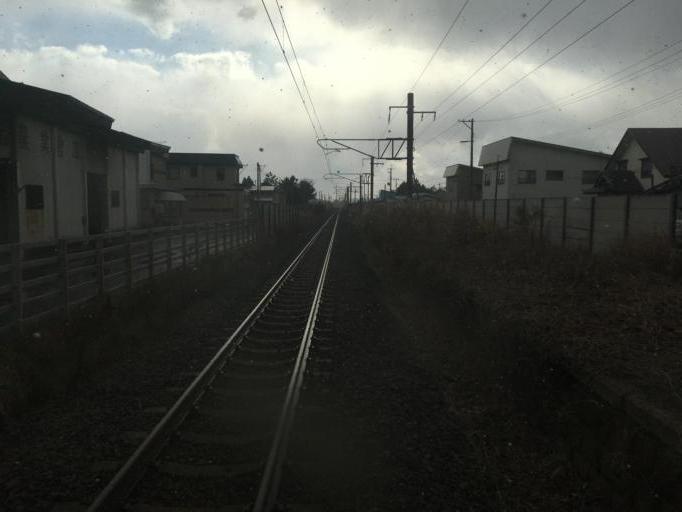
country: JP
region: Aomori
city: Aomori Shi
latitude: 40.9682
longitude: 140.6551
